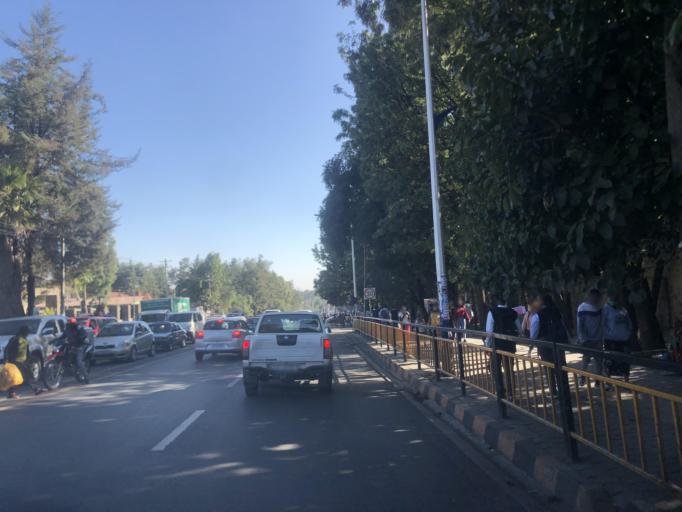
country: ET
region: Adis Abeba
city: Addis Ababa
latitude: 9.0374
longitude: 38.7627
